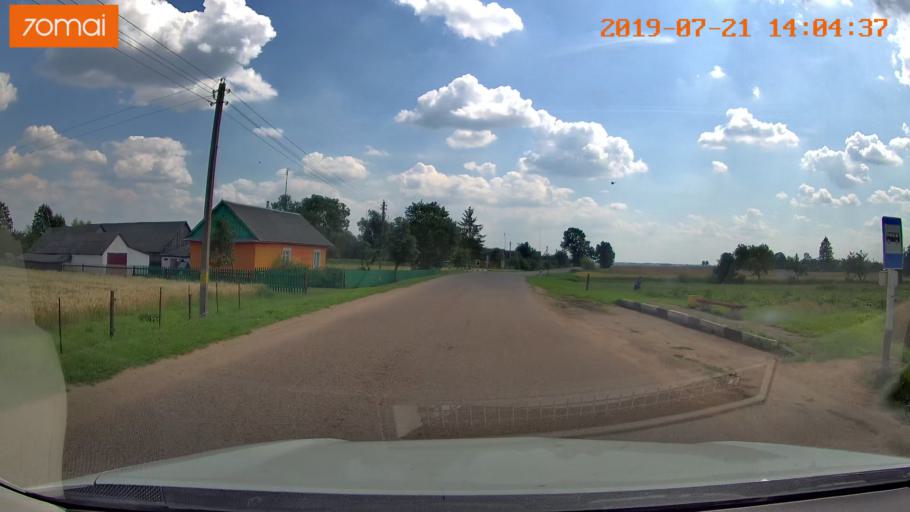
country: BY
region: Grodnenskaya
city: Lyubcha
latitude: 53.7190
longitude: 26.1007
